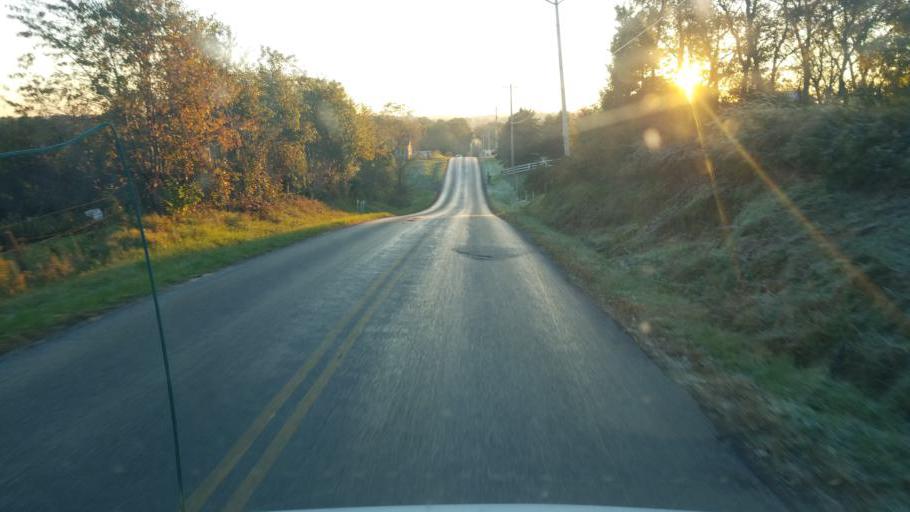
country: US
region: Ohio
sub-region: Stark County
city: Brewster
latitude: 40.6534
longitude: -81.7251
